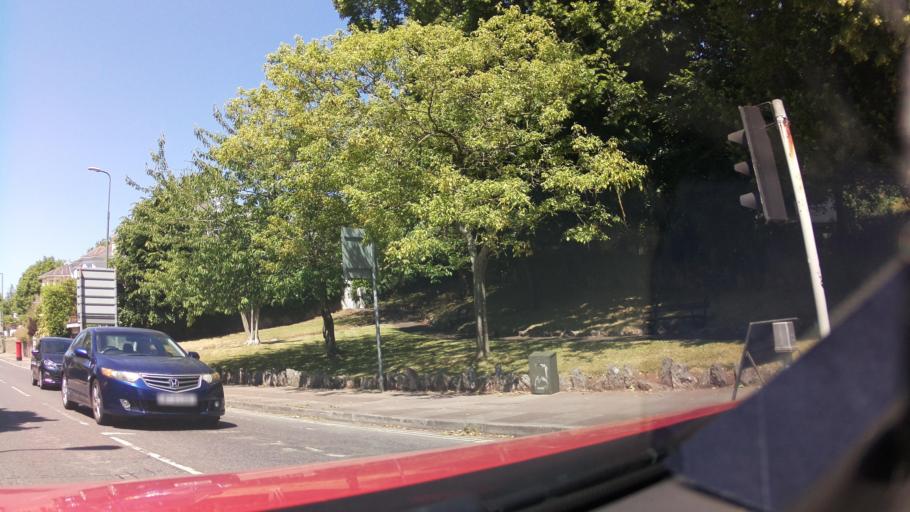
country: GB
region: England
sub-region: Borough of Torbay
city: Torquay
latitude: 50.4648
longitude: -3.5421
